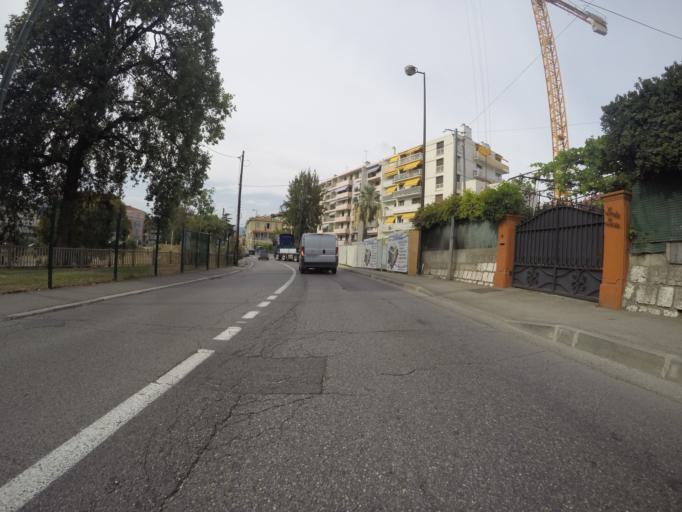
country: FR
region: Provence-Alpes-Cote d'Azur
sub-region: Departement des Alpes-Maritimes
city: Cagnes-sur-Mer
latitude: 43.6621
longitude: 7.1548
